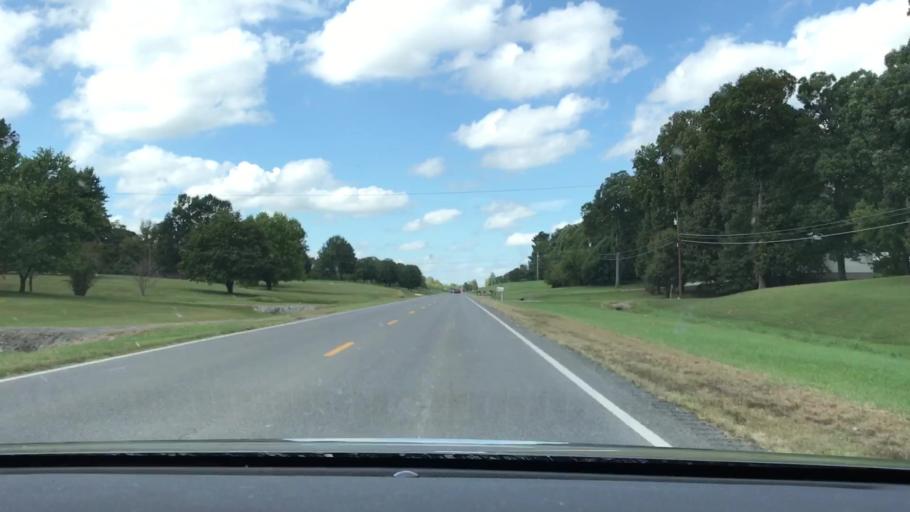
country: US
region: Kentucky
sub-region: Livingston County
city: Ledbetter
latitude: 37.0077
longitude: -88.4858
